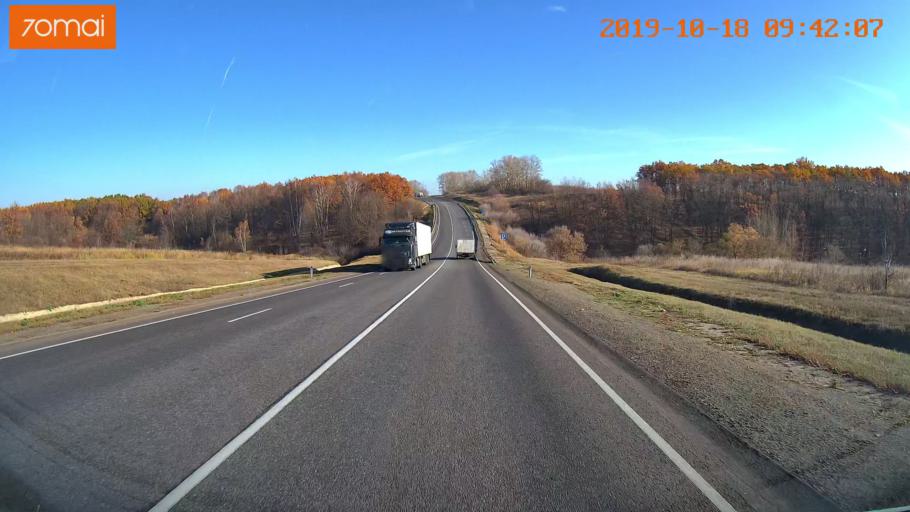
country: RU
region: Tula
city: Kazachka
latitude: 53.2832
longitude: 38.1722
